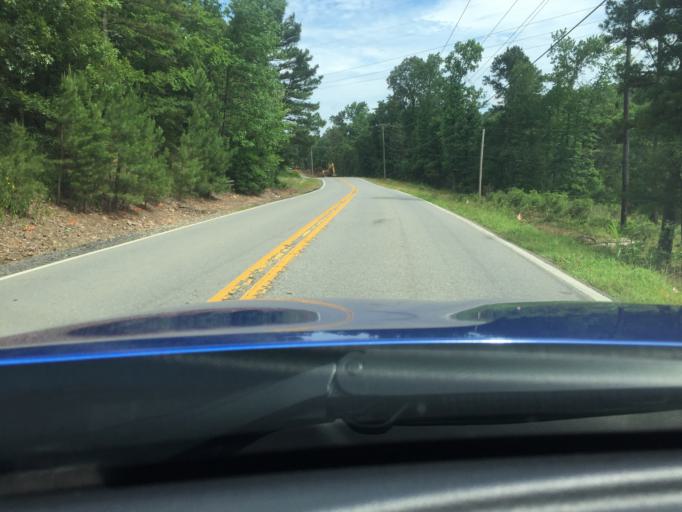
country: US
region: Arkansas
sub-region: Pulaski County
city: Maumelle
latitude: 34.8106
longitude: -92.4428
